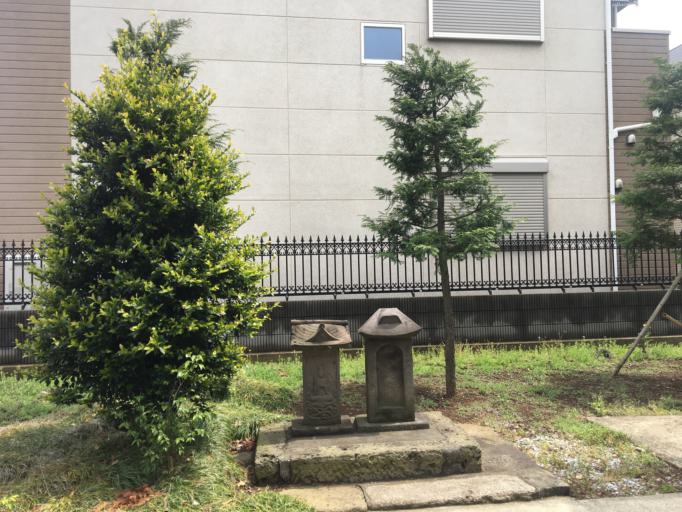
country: JP
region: Saitama
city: Shiki
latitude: 35.8357
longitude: 139.5591
